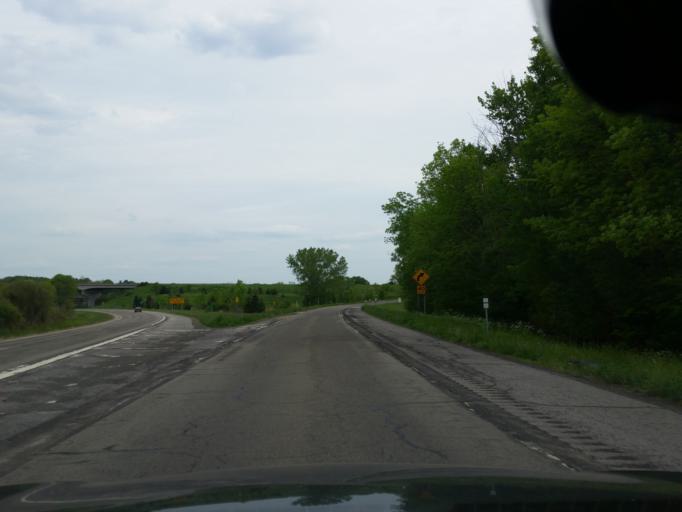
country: US
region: New York
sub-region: Chautauqua County
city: Lakewood
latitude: 42.1570
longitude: -79.3777
